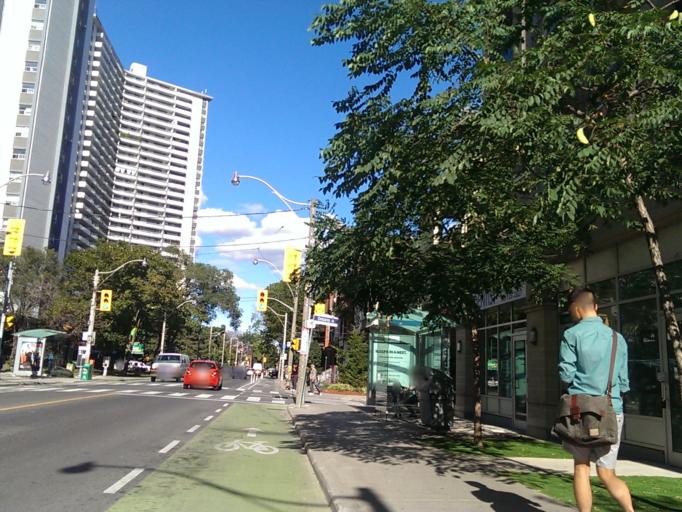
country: CA
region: Ontario
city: Toronto
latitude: 43.6675
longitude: -79.3725
